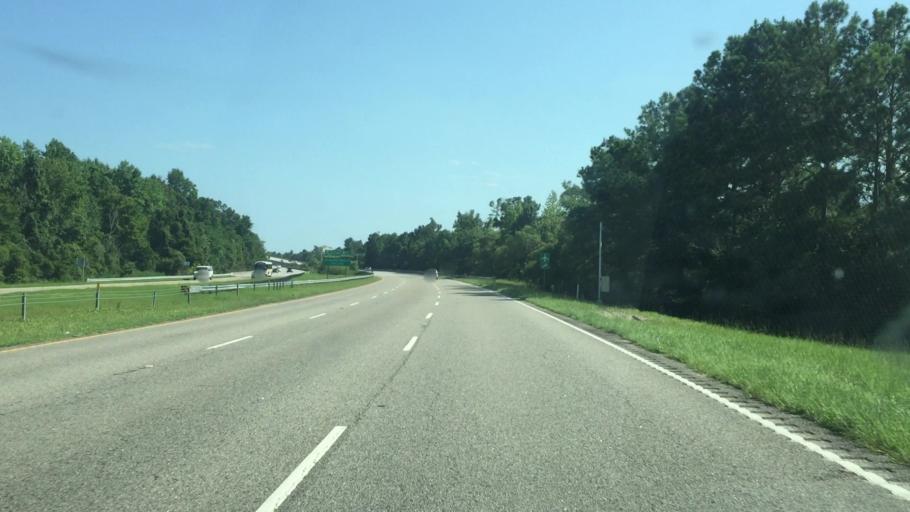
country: US
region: South Carolina
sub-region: Horry County
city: North Myrtle Beach
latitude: 33.7995
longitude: -78.7795
